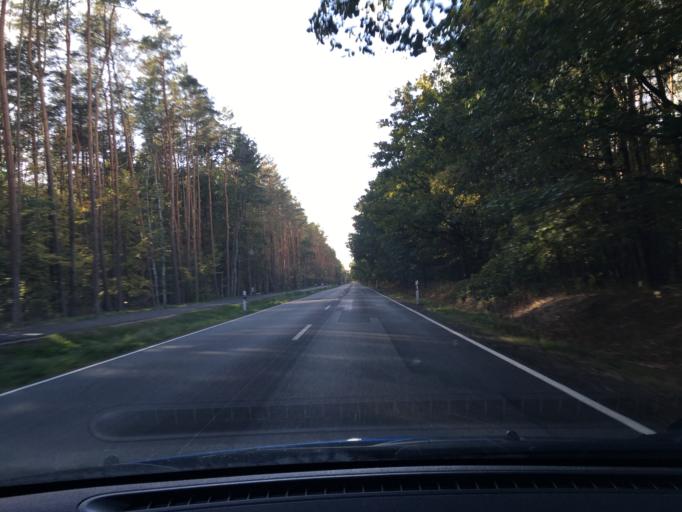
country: DE
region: Mecklenburg-Vorpommern
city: Boizenburg
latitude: 53.3821
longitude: 10.8695
